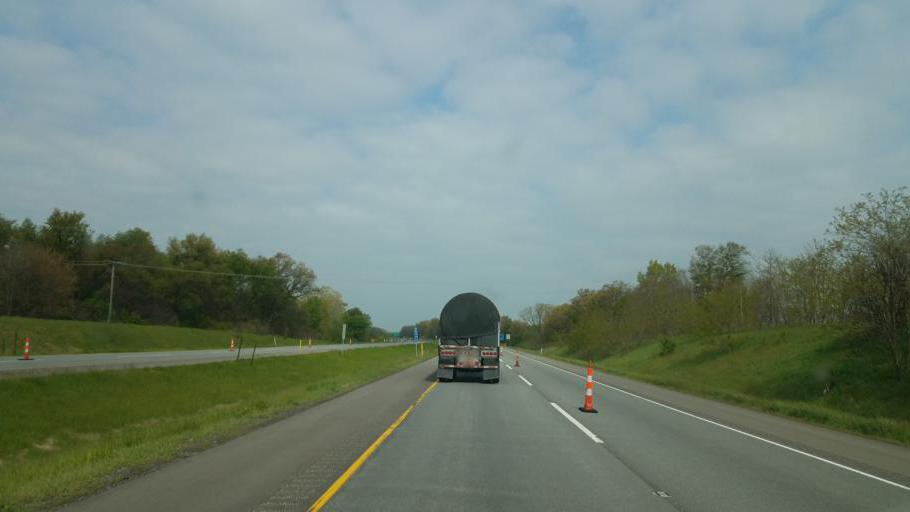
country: US
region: Indiana
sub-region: Saint Joseph County
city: South Bend
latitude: 41.7257
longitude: -86.2991
